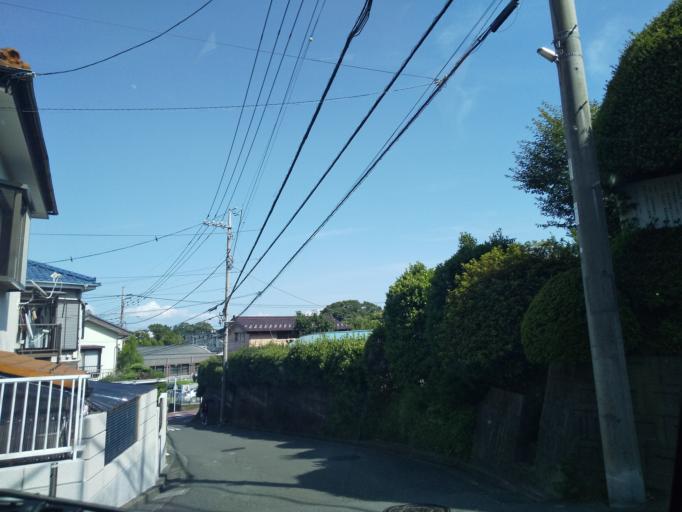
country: JP
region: Kanagawa
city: Minami-rinkan
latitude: 35.4604
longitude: 139.4188
